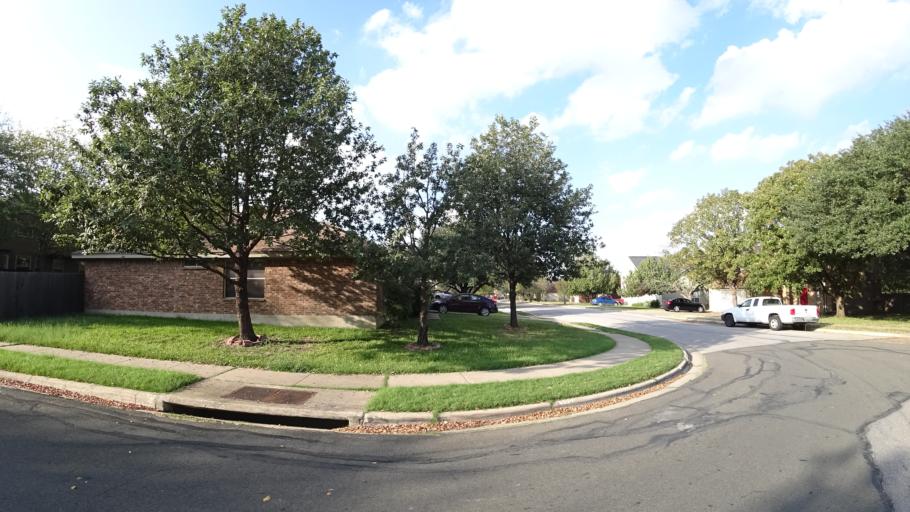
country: US
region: Texas
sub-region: Williamson County
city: Round Rock
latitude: 30.4926
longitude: -97.6616
